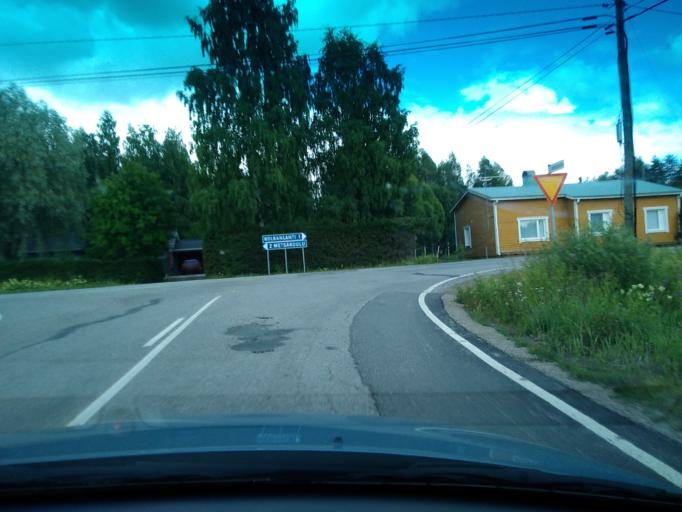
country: FI
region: Central Finland
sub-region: Saarijaervi-Viitasaari
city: Saarijaervi
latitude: 62.7380
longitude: 25.1731
